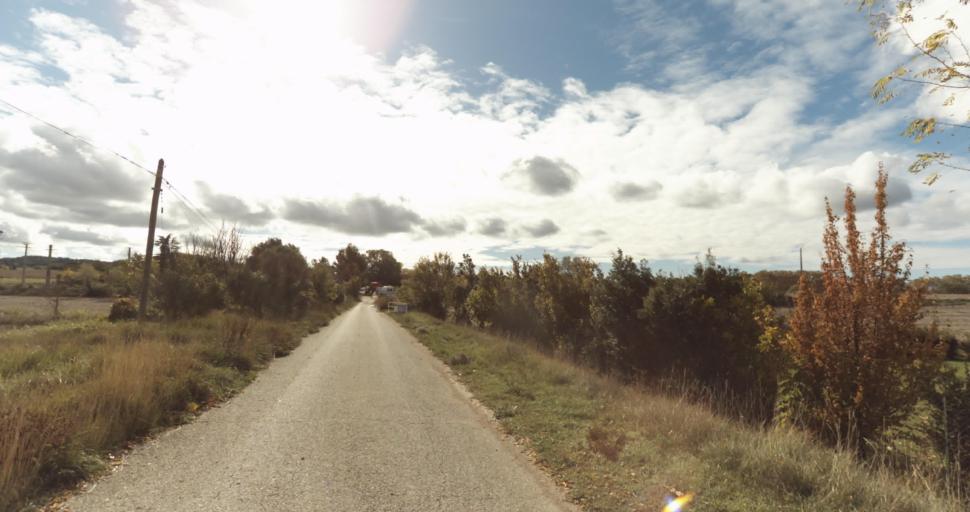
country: FR
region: Provence-Alpes-Cote d'Azur
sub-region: Departement des Bouches-du-Rhone
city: Venelles
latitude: 43.5852
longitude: 5.4846
